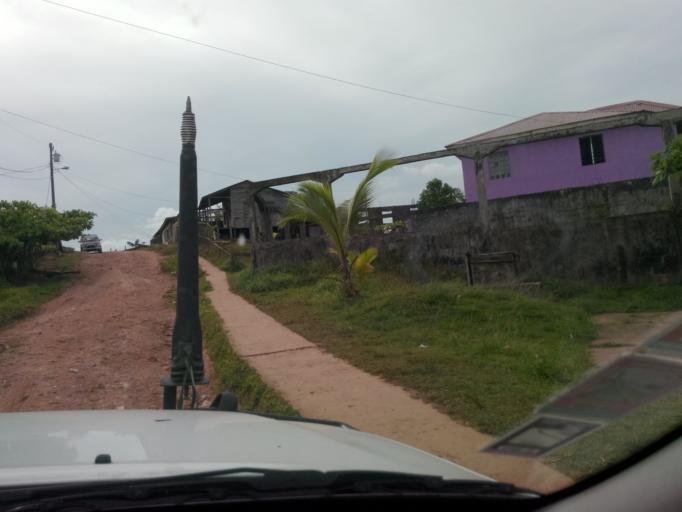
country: NI
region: Atlantico Sur
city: Bluefields
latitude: 12.0276
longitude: -83.7734
